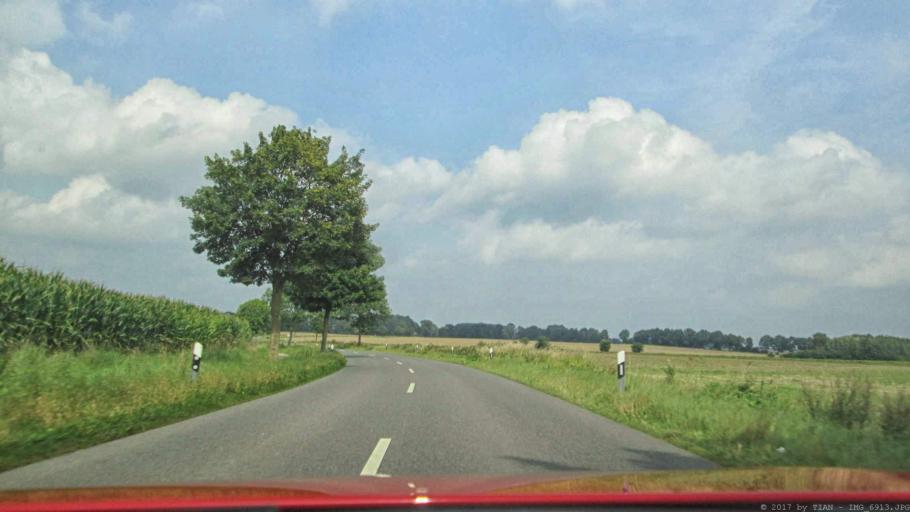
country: DE
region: Lower Saxony
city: Altenmedingen
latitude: 53.1340
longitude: 10.6080
